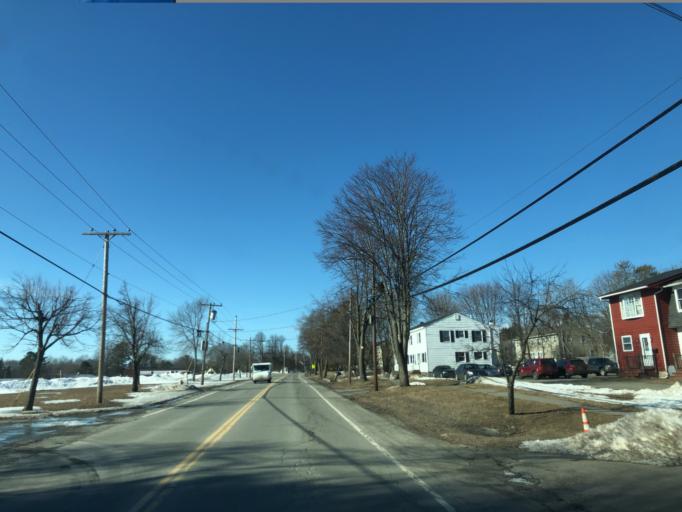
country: US
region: Maine
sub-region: Penobscot County
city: Brewer
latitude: 44.8160
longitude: -68.7548
